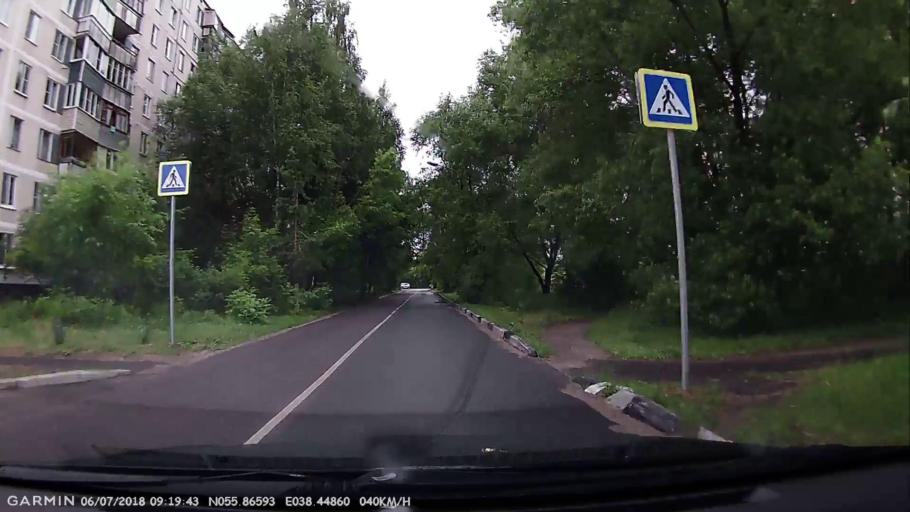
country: RU
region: Moskovskaya
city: Noginsk
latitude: 55.8660
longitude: 38.4485
